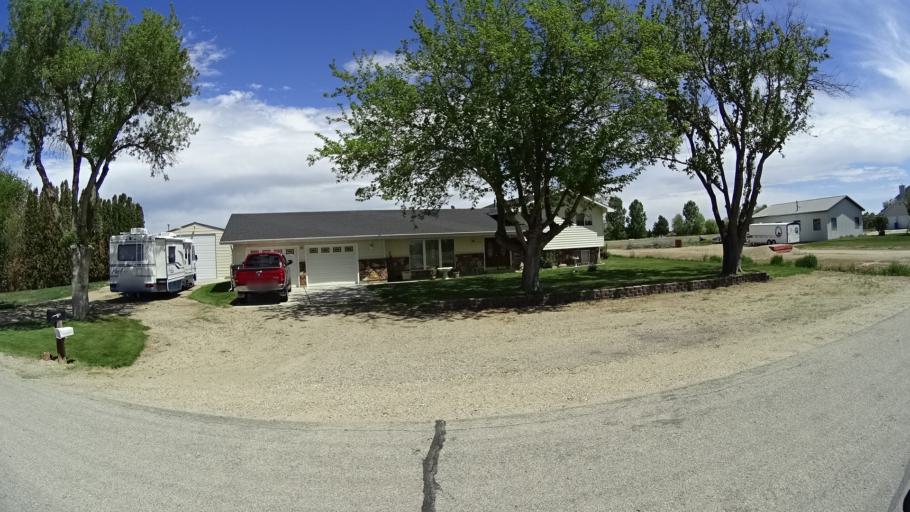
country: US
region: Idaho
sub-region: Ada County
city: Meridian
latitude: 43.5740
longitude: -116.3465
